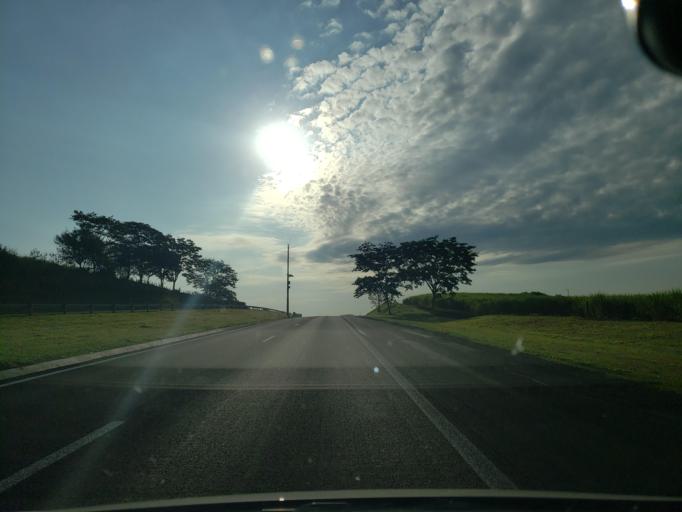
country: BR
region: Sao Paulo
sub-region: Valparaiso
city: Valparaiso
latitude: -21.1931
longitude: -50.9054
